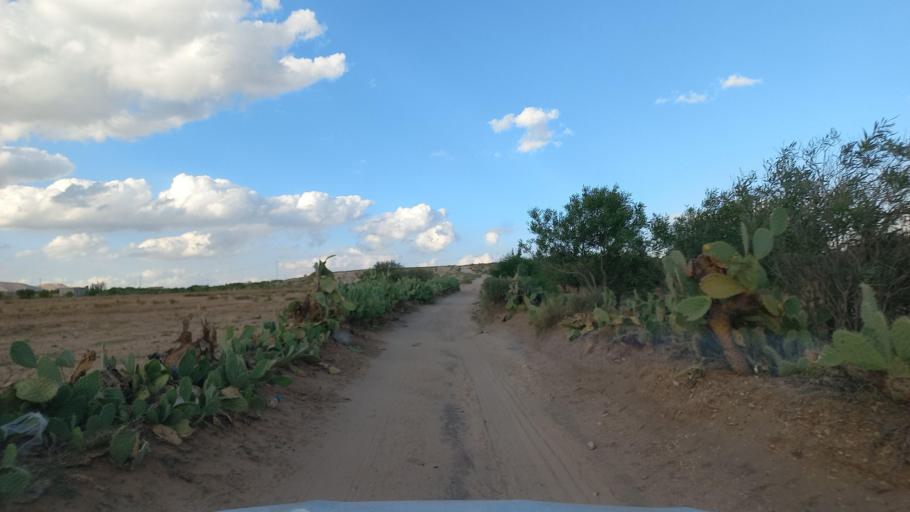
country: TN
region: Al Qasrayn
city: Sbiba
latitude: 35.3874
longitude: 9.0539
